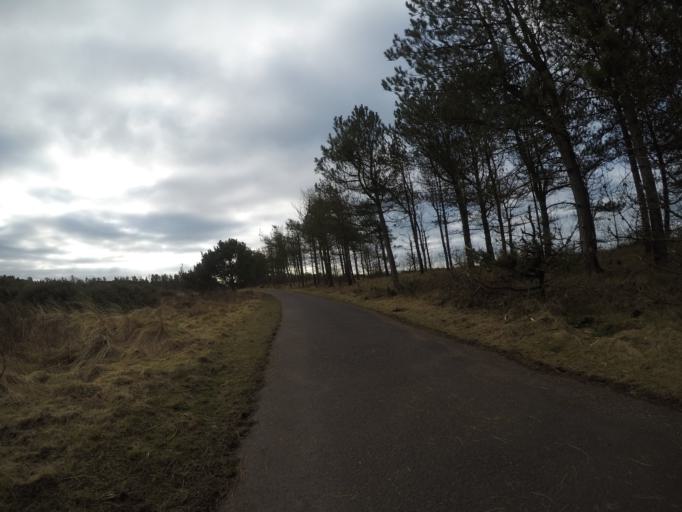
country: GB
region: Scotland
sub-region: North Ayrshire
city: Irvine
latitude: 55.5941
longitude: -4.6720
